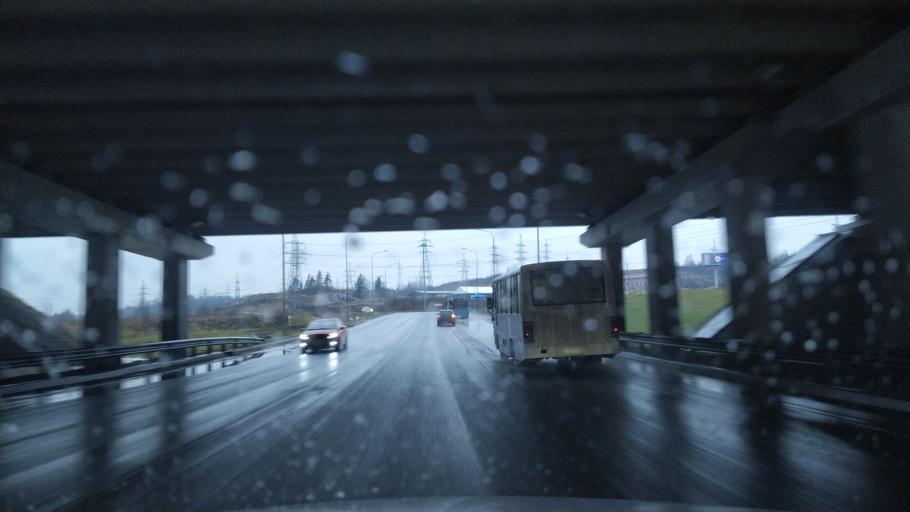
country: RU
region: Leningrad
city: Bugry
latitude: 60.0966
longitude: 30.3799
